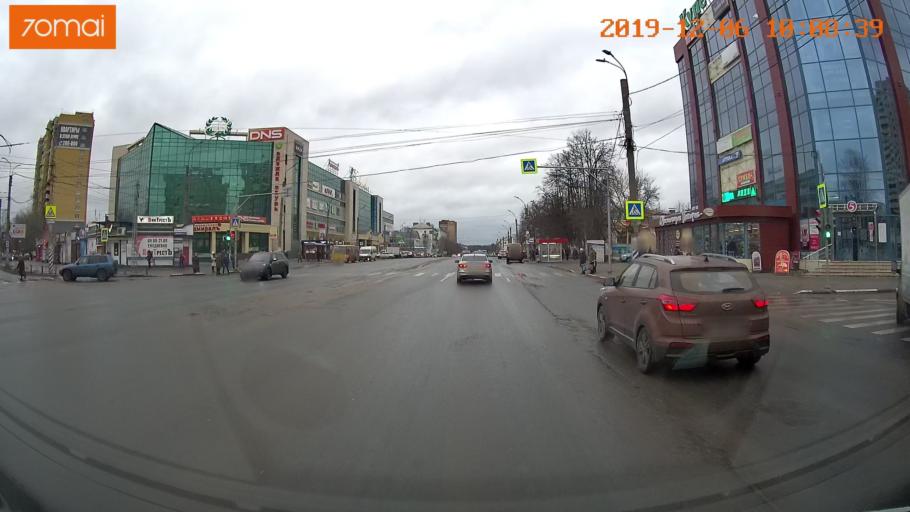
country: RU
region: Ivanovo
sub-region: Gorod Ivanovo
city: Ivanovo
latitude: 57.0168
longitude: 40.9696
